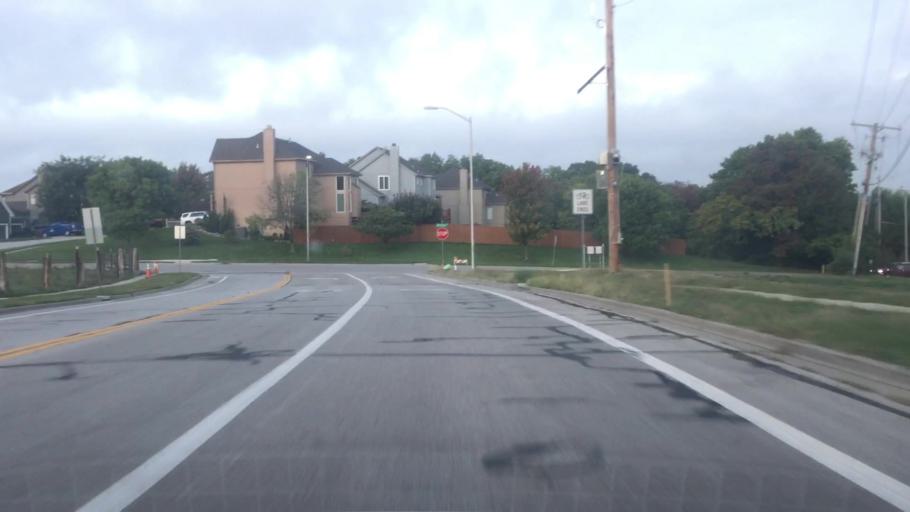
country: US
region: Kansas
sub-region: Johnson County
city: Shawnee
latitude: 39.0365
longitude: -94.7497
